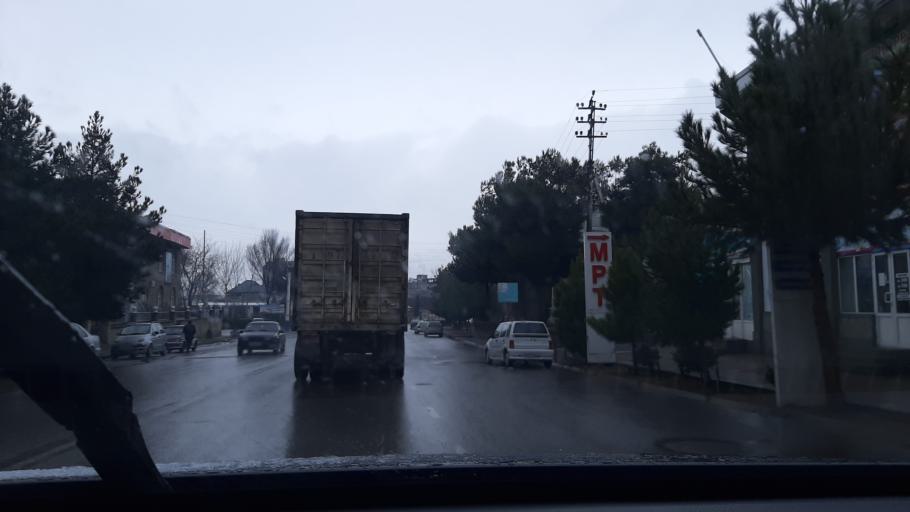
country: TJ
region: Viloyati Sughd
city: Khujand
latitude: 40.2734
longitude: 69.6422
